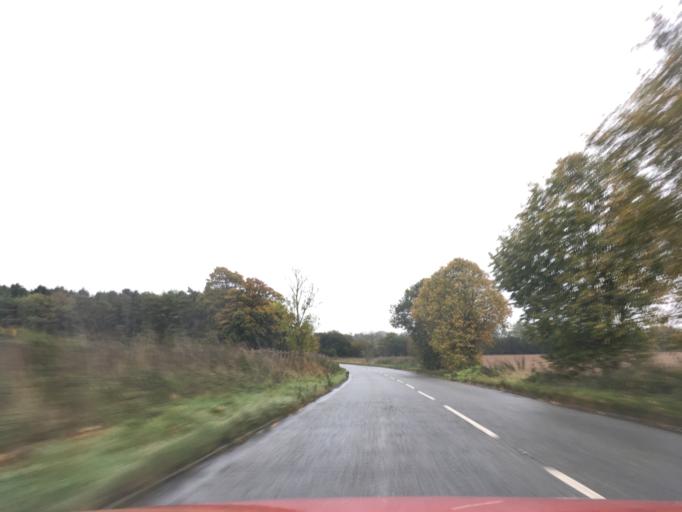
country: GB
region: England
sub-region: West Berkshire
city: Wickham
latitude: 51.4501
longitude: -1.4554
